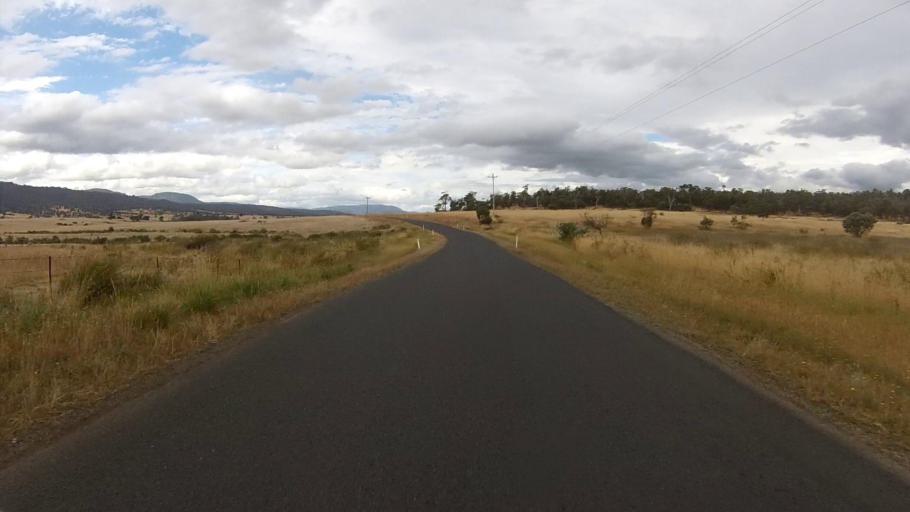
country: AU
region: Tasmania
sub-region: Northern Midlands
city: Evandale
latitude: -41.8248
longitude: 147.8056
